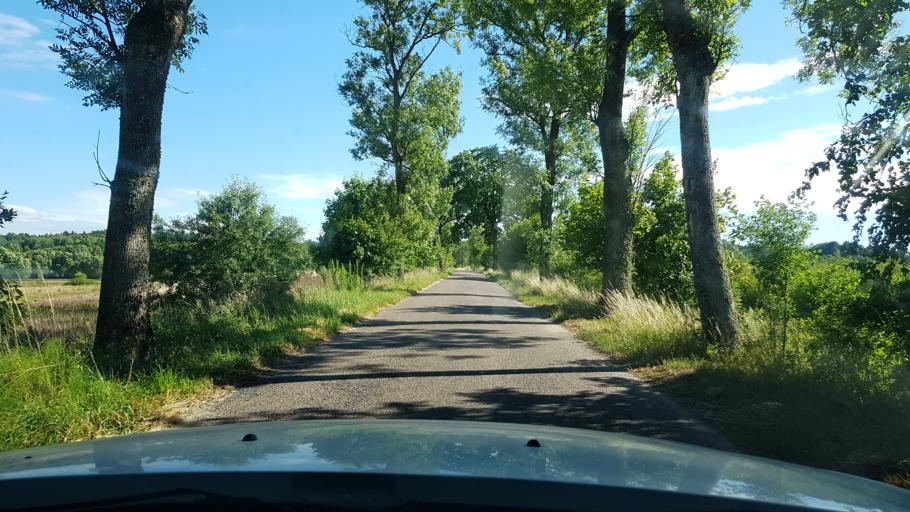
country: PL
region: West Pomeranian Voivodeship
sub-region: Powiat swidwinski
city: Polczyn-Zdroj
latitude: 53.7461
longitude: 16.0847
